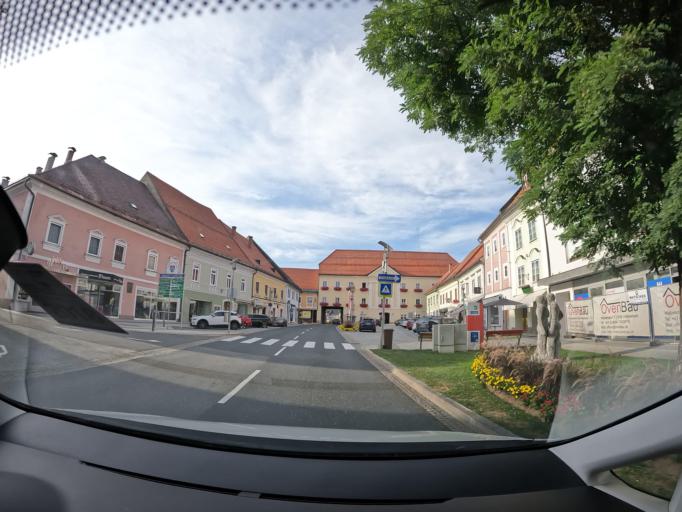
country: AT
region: Carinthia
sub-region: Politischer Bezirk Volkermarkt
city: Voelkermarkt
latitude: 46.6597
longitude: 14.6343
